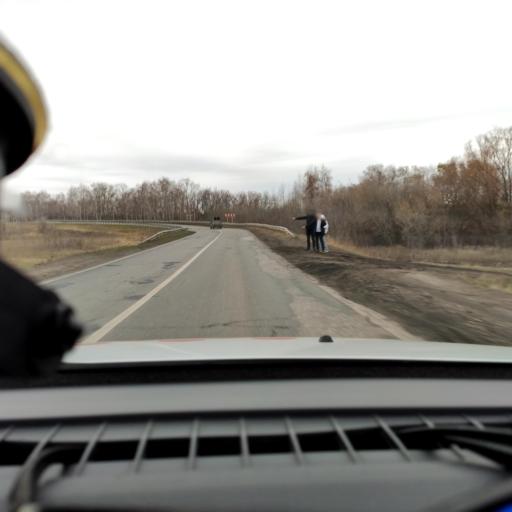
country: RU
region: Samara
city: Smyshlyayevka
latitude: 53.1373
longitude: 50.3743
